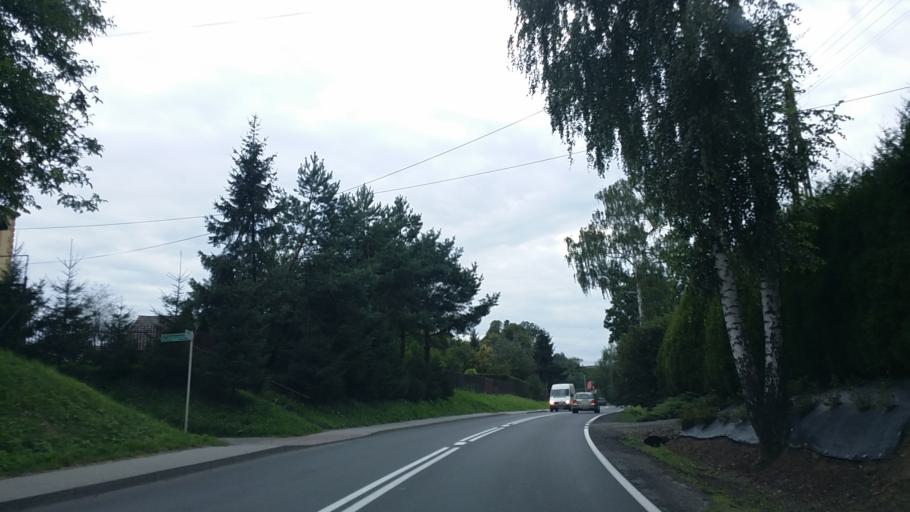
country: PL
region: Lesser Poland Voivodeship
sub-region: Powiat wadowicki
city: Brzeznica
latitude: 49.9651
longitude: 19.6248
